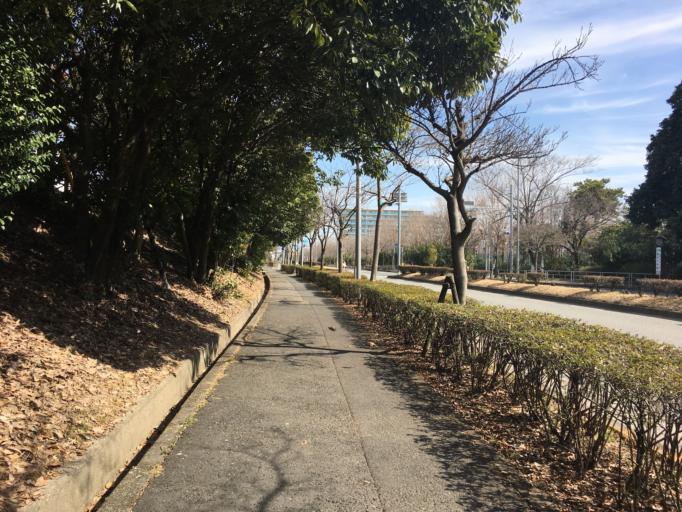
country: JP
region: Osaka
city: Mino
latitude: 34.8137
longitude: 135.4992
